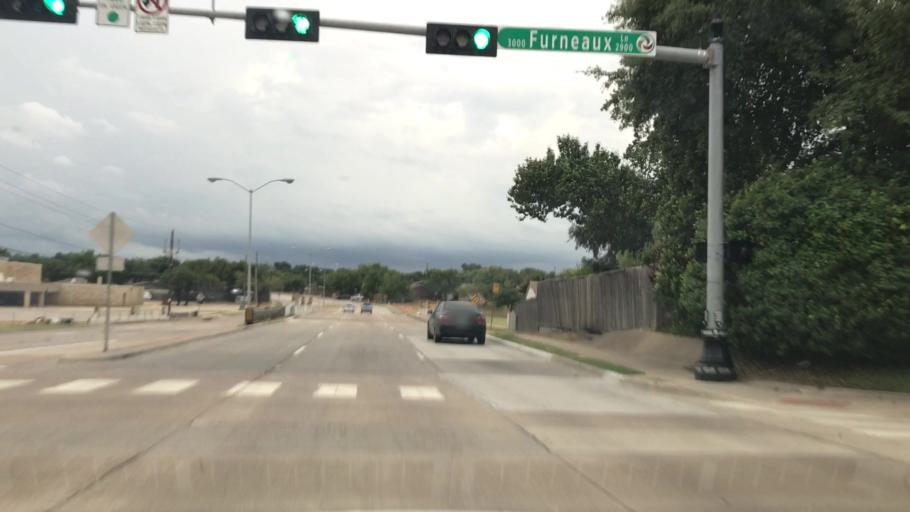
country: US
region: Texas
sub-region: Dallas County
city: Carrollton
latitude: 32.9993
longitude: -96.8798
